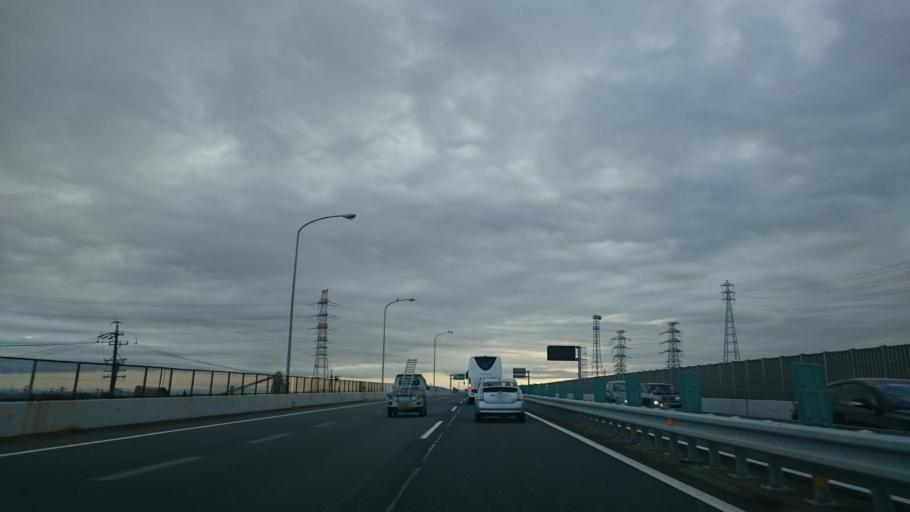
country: JP
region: Aichi
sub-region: Aisai-shi
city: Aisai
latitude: 35.1286
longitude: 136.7323
